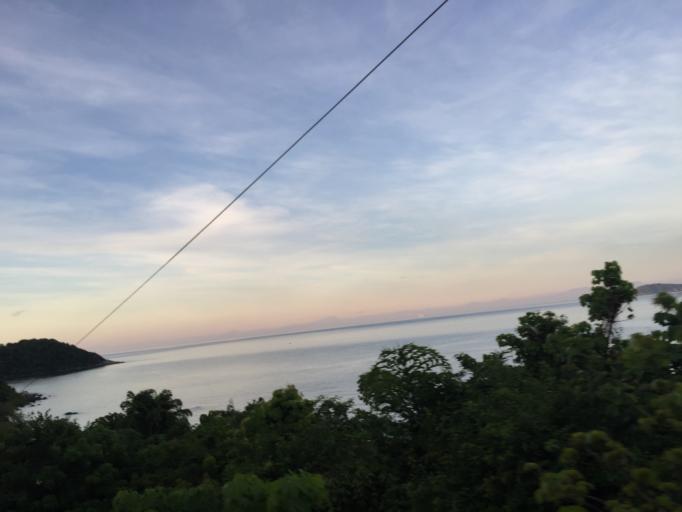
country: VN
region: Quang Nam
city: Hoi An
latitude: 15.9516
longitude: 108.5086
